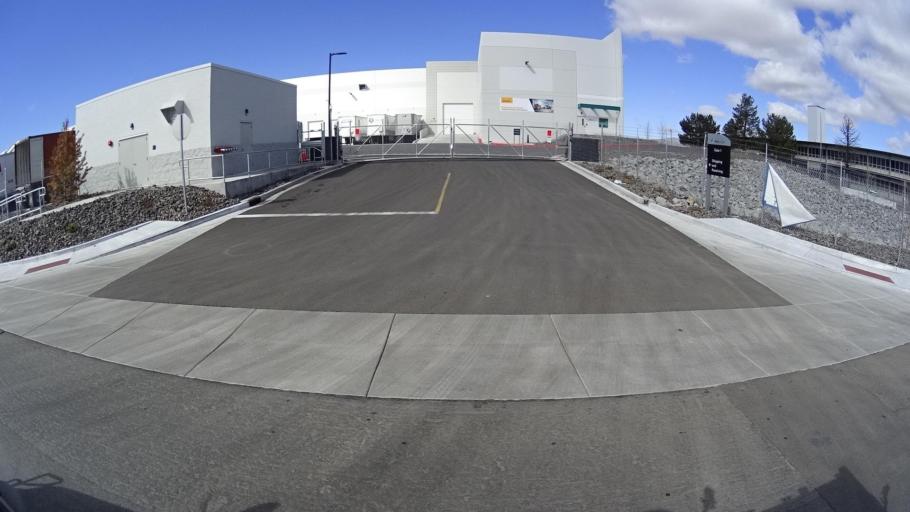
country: US
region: Nevada
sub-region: Washoe County
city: Lemmon Valley
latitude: 39.6555
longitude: -119.8695
